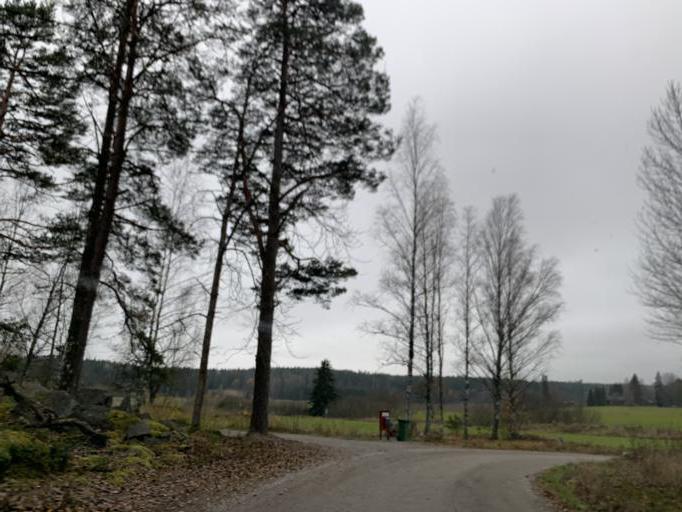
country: SE
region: Vaestmanland
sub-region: Surahammars Kommun
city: Ramnas
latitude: 59.7427
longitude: 16.1516
